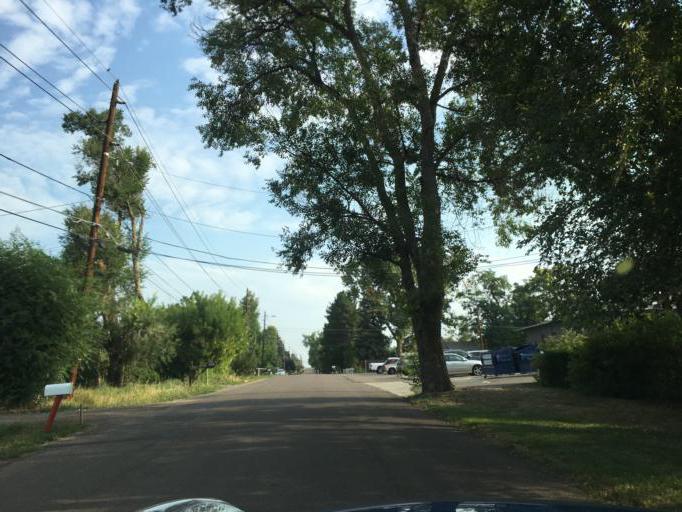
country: US
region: Colorado
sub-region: Jefferson County
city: Wheat Ridge
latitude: 39.7423
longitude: -105.1065
